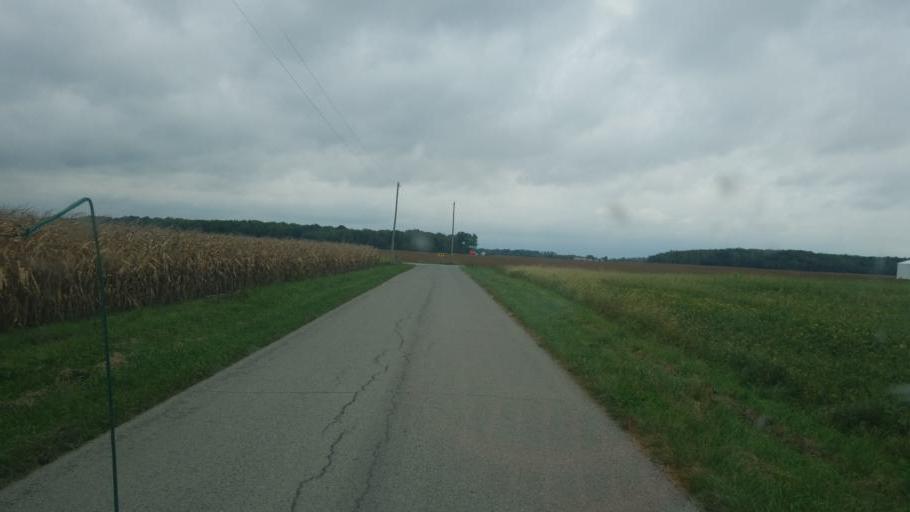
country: US
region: Ohio
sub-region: Seneca County
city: Fostoria
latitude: 41.0782
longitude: -83.4959
